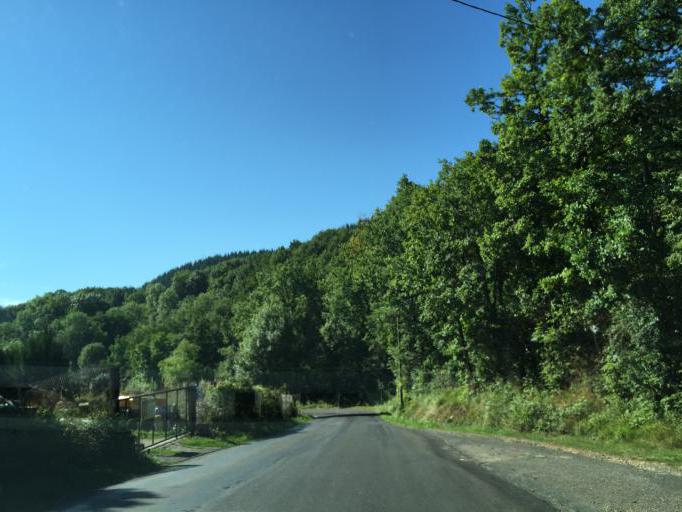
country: FR
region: Midi-Pyrenees
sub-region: Departement de l'Aveyron
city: Laissac
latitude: 44.3768
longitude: 2.8083
